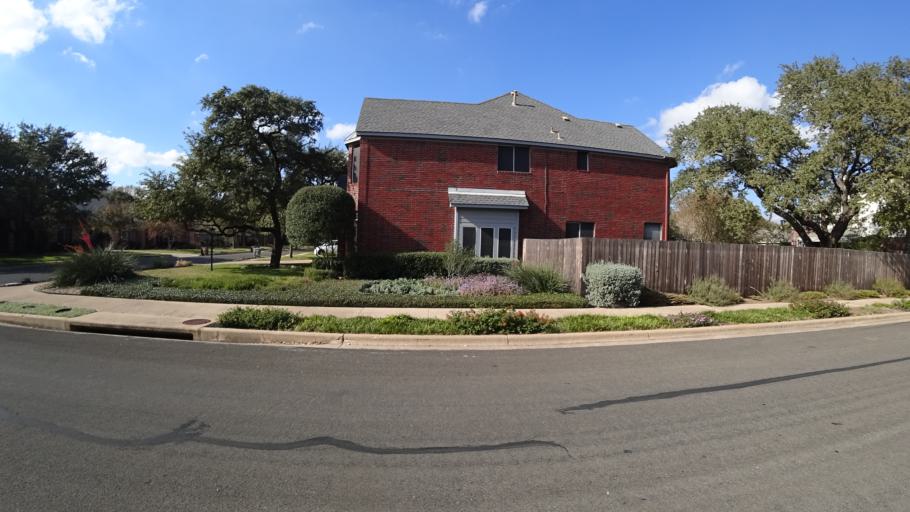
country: US
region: Texas
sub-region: Travis County
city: Shady Hollow
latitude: 30.1788
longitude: -97.8552
